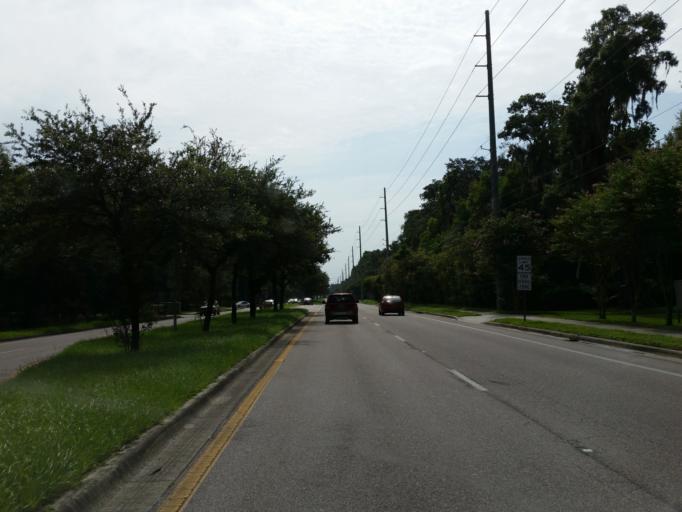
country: US
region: Florida
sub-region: Hillsborough County
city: Bloomingdale
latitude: 27.8937
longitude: -82.2536
